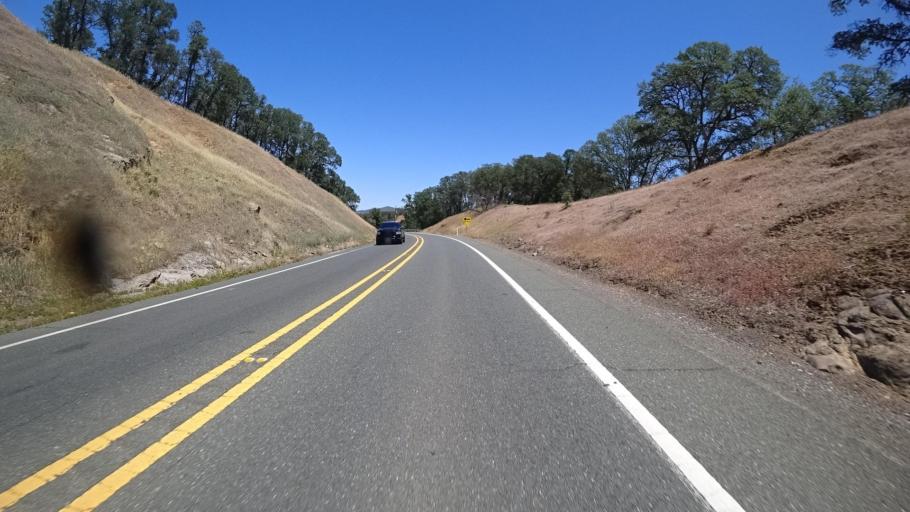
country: US
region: California
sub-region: Lake County
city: Lower Lake
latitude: 38.8837
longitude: -122.6055
